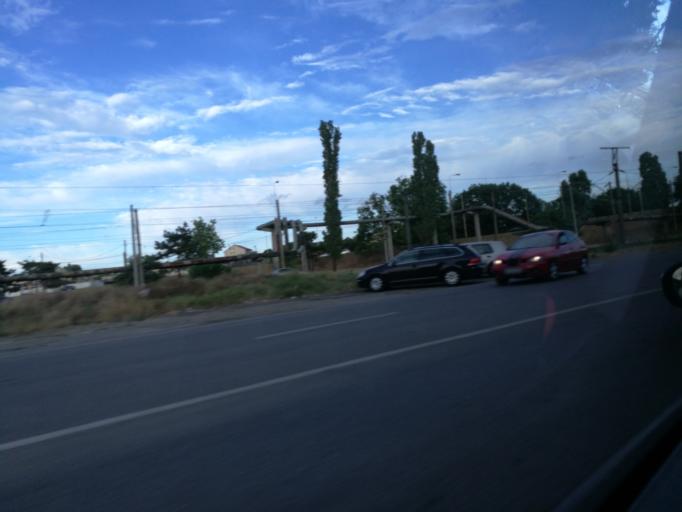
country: RO
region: Constanta
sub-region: Municipiul Constanta
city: Constanta
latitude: 44.1501
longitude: 28.6252
